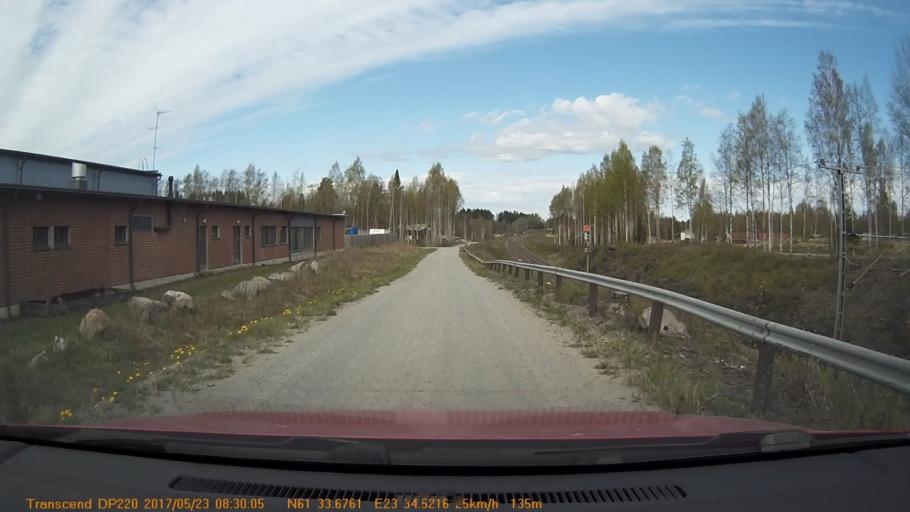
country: FI
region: Pirkanmaa
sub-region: Tampere
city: Yloejaervi
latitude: 61.5613
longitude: 23.5753
